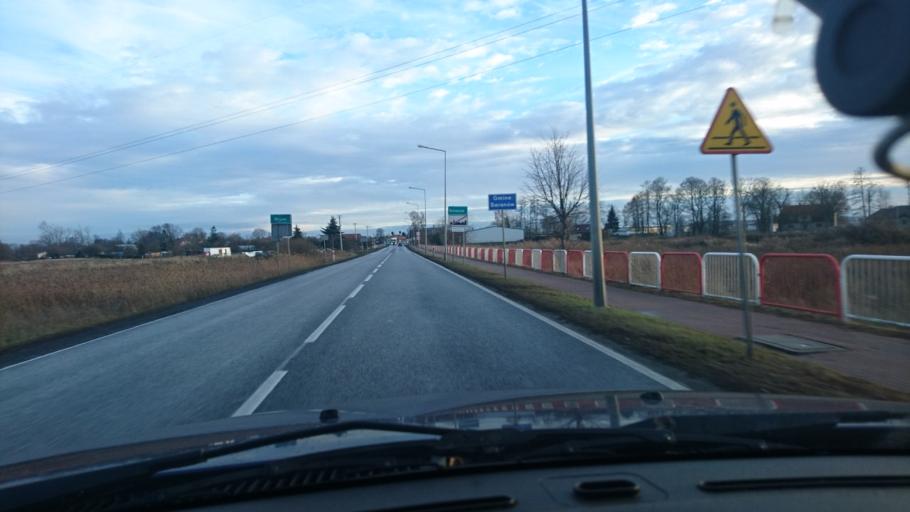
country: PL
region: Greater Poland Voivodeship
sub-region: Powiat kepinski
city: Kepno
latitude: 51.2710
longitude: 17.9941
